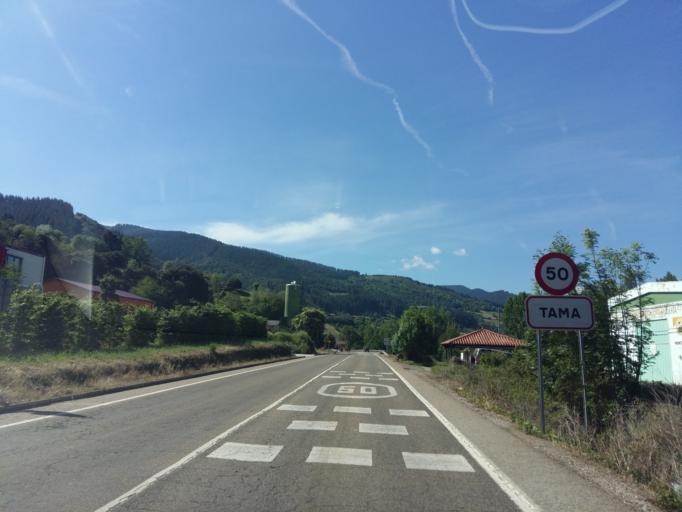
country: ES
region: Cantabria
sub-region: Provincia de Cantabria
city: Potes
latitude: 43.1810
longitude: -4.6012
